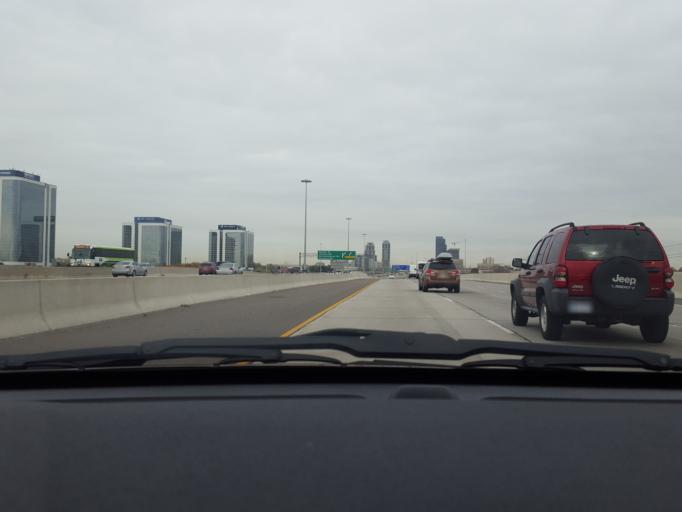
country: CA
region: Ontario
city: Etobicoke
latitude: 43.6223
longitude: -79.5536
